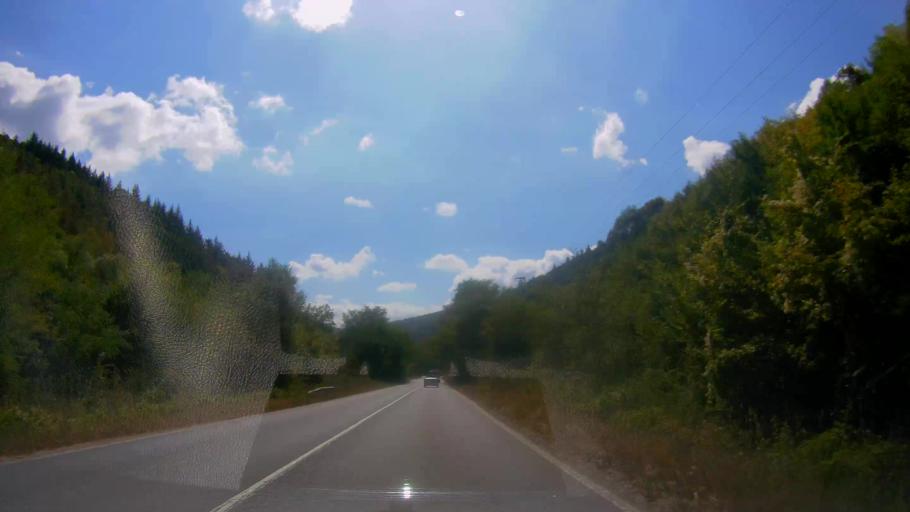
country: BG
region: Stara Zagora
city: Gurkovo
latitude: 42.7488
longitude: 25.7098
